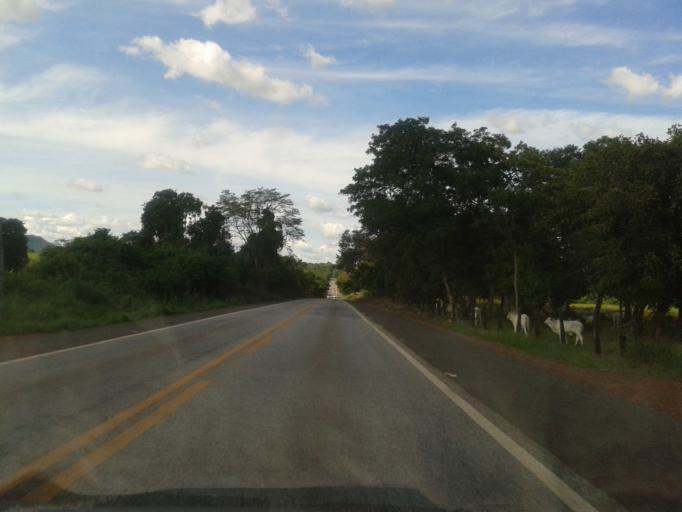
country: BR
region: Goias
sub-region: Mozarlandia
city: Mozarlandia
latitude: -14.9672
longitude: -50.5799
